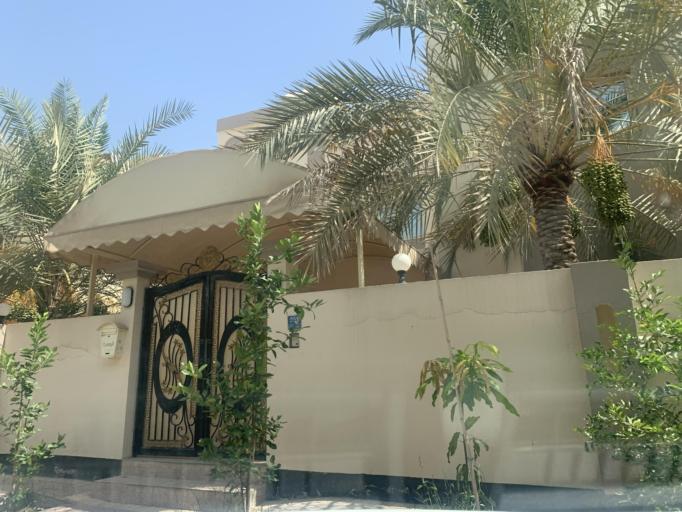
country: BH
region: Manama
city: Jidd Hafs
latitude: 26.2261
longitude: 50.5487
